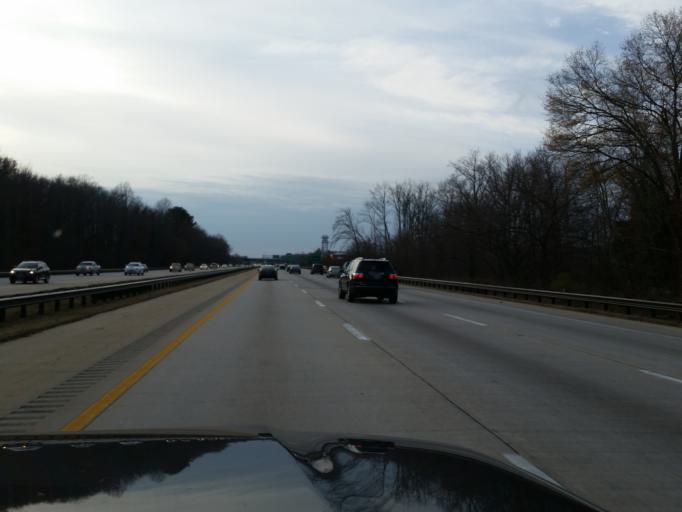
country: US
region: Maryland
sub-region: Prince George's County
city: Bowie
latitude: 38.9557
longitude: -76.6996
